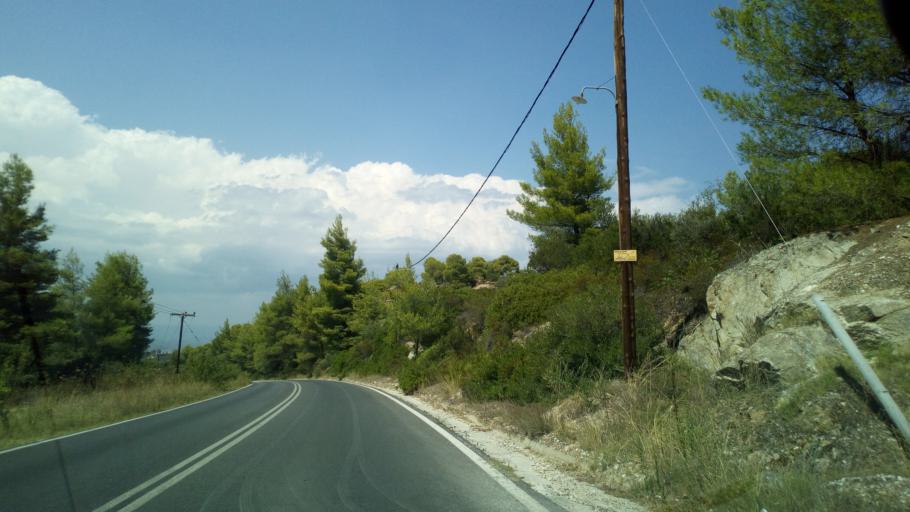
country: GR
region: Central Macedonia
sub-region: Nomos Chalkidikis
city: Agios Nikolaos
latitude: 40.2120
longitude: 23.7564
